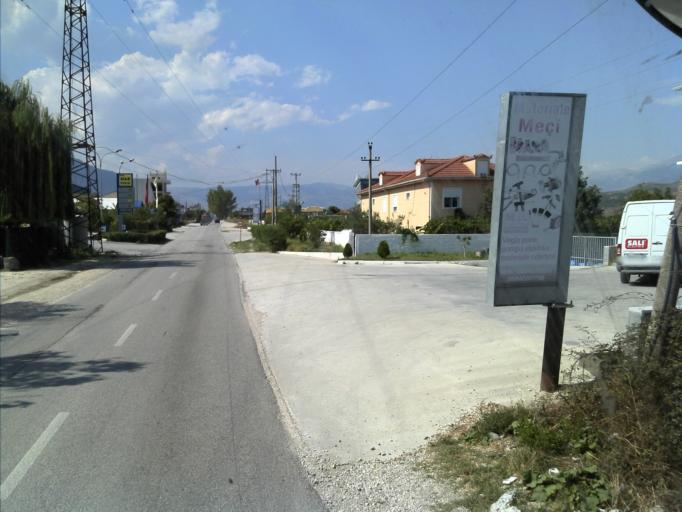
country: AL
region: Gjirokaster
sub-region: Rrethi i Gjirokastres
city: Lazarat
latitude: 40.0662
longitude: 20.1645
